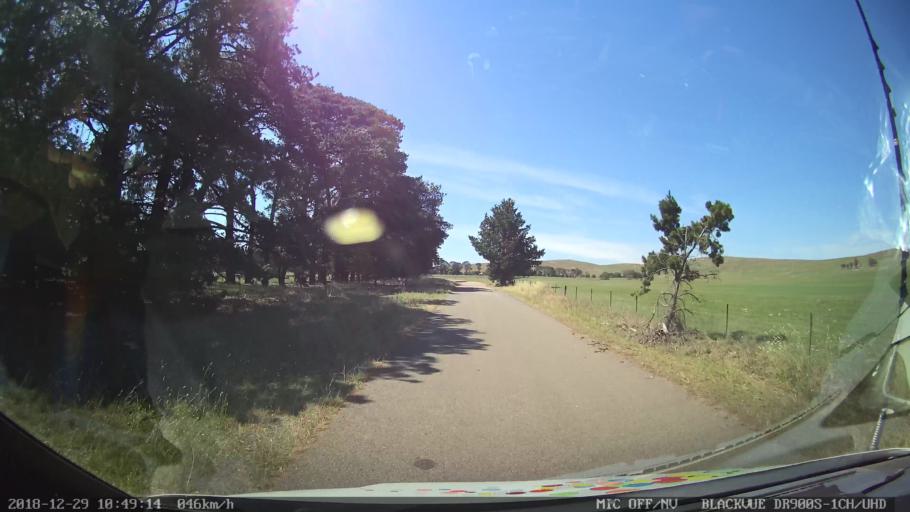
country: AU
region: New South Wales
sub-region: Palerang
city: Bungendore
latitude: -35.0742
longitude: 149.5148
